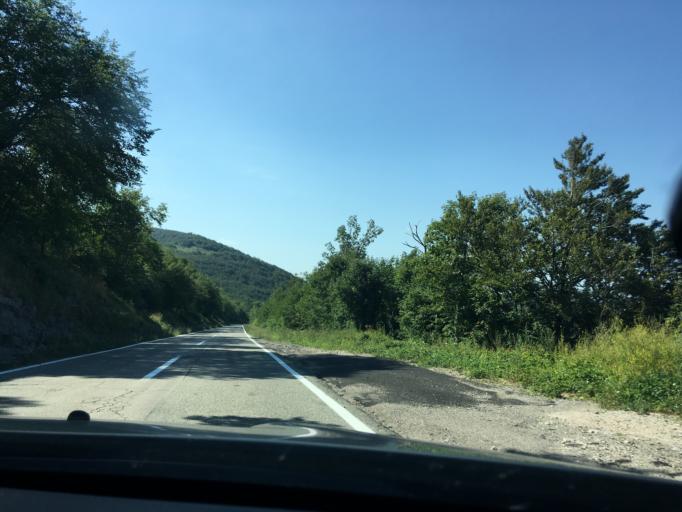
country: HR
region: Primorsko-Goranska
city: Hreljin
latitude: 45.3586
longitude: 14.6166
